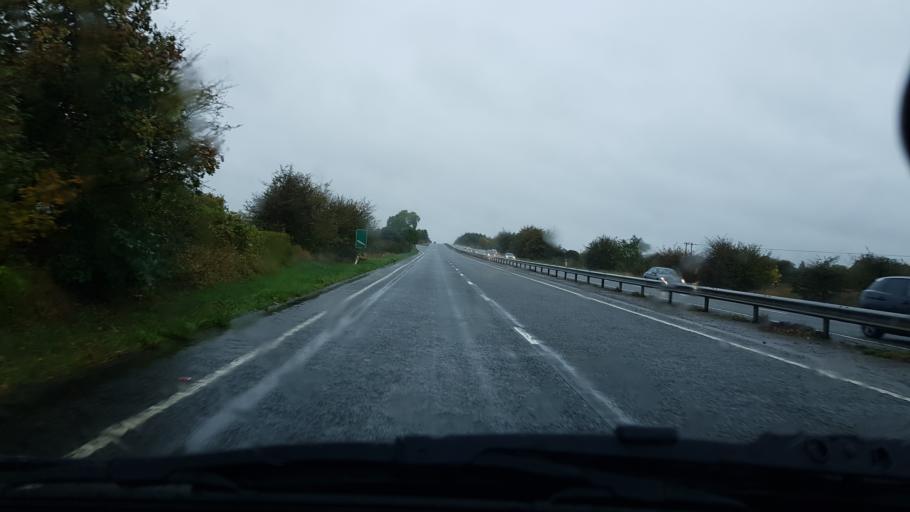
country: GB
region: England
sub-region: Oxfordshire
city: Carterton
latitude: 51.7816
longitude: -1.5455
